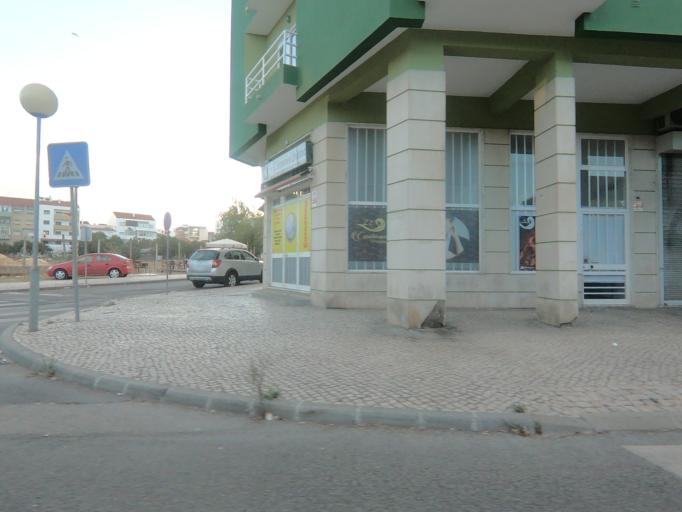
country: PT
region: Setubal
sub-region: Moita
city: Alhos Vedros
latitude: 38.6606
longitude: -9.0419
